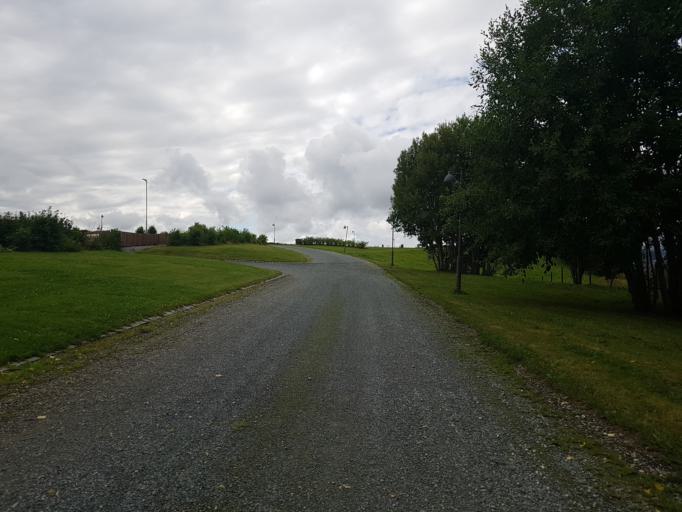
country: NO
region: Sor-Trondelag
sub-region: Trondheim
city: Trondheim
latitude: 63.3838
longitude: 10.4125
